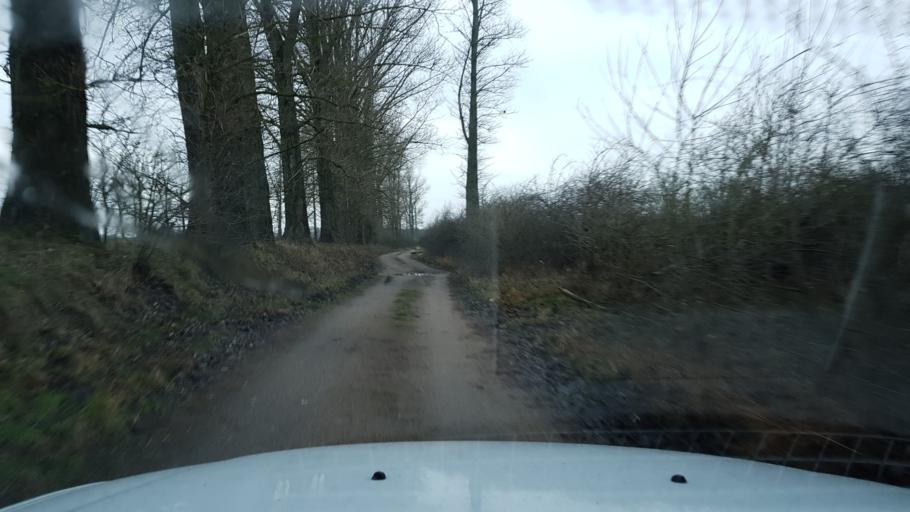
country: PL
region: West Pomeranian Voivodeship
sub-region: Powiat gryficki
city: Brojce
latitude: 53.9820
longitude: 15.3084
